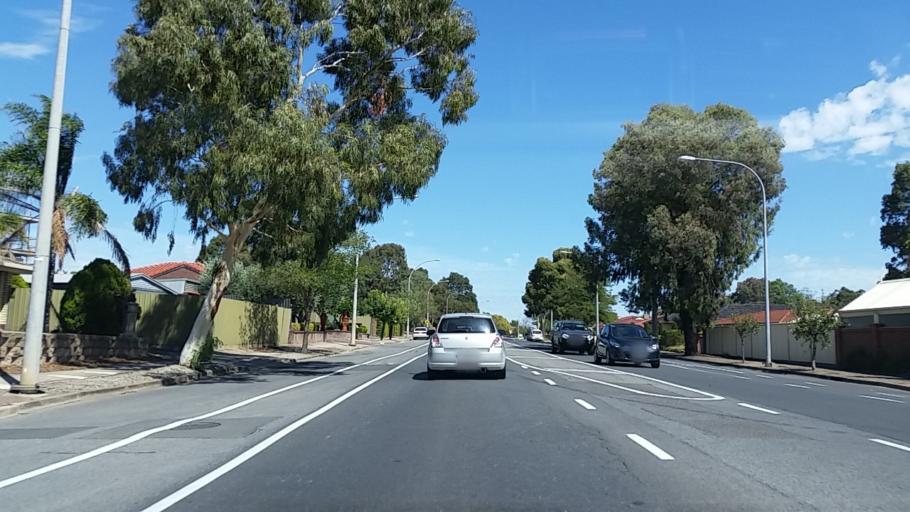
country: AU
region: South Australia
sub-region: Campbelltown
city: Athelstone
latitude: -34.8758
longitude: 138.6951
